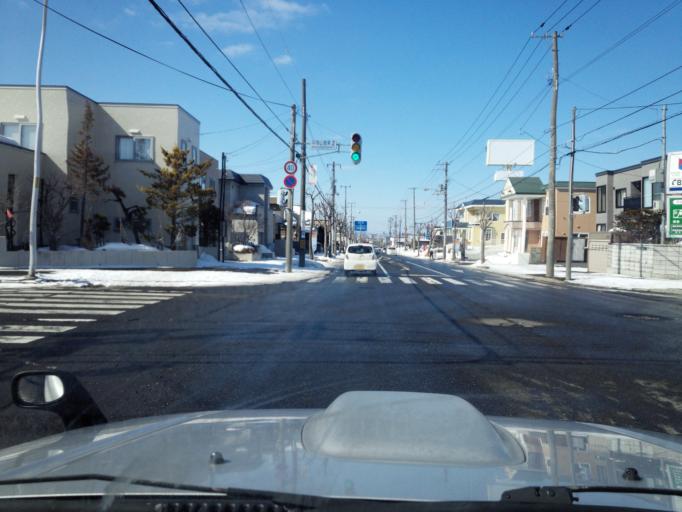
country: JP
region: Hokkaido
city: Kitahiroshima
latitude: 43.0109
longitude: 141.4720
